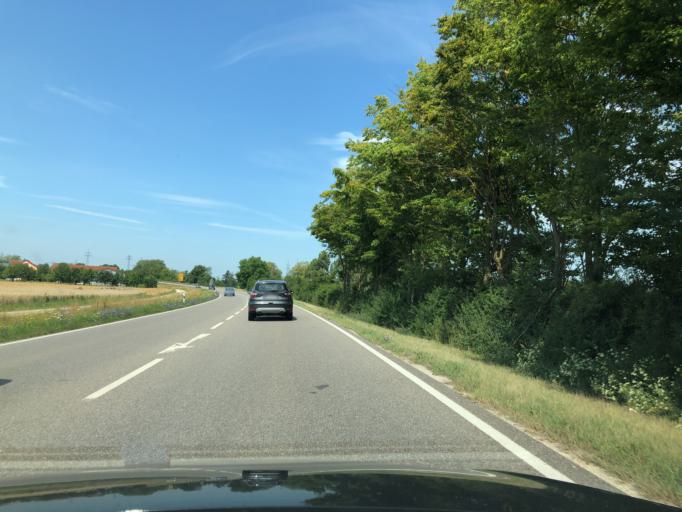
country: DE
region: Bavaria
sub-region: Upper Bavaria
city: Manching
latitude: 48.7167
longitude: 11.4593
